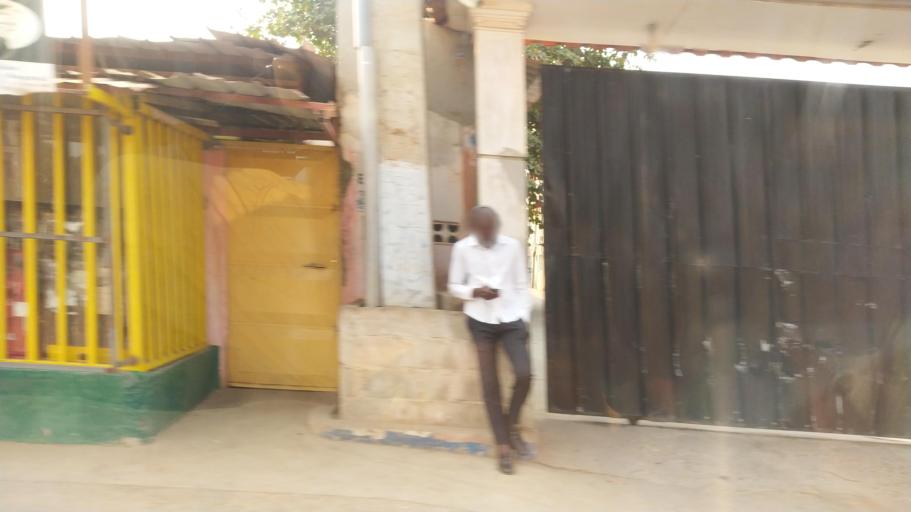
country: AO
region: Luanda
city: Luanda
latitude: -8.8959
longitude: 13.1979
